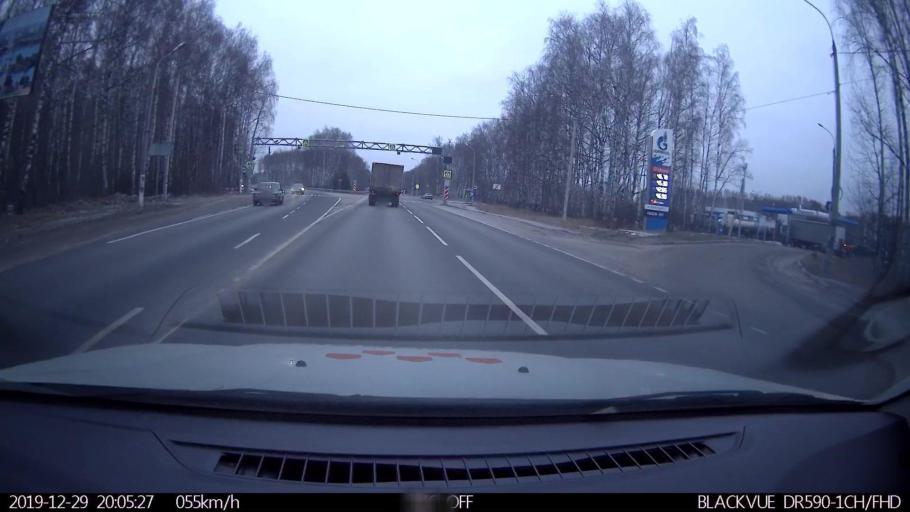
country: RU
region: Nizjnij Novgorod
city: Neklyudovo
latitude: 56.3914
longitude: 44.0105
